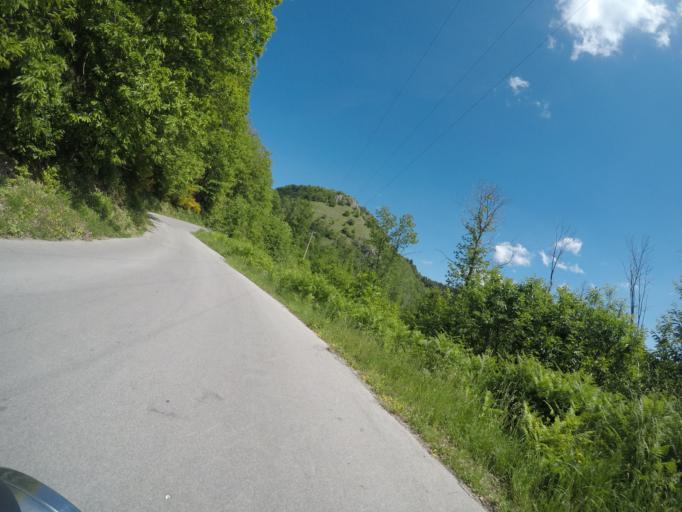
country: IT
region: Tuscany
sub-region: Provincia di Lucca
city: Careggine
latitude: 44.0926
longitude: 10.3254
